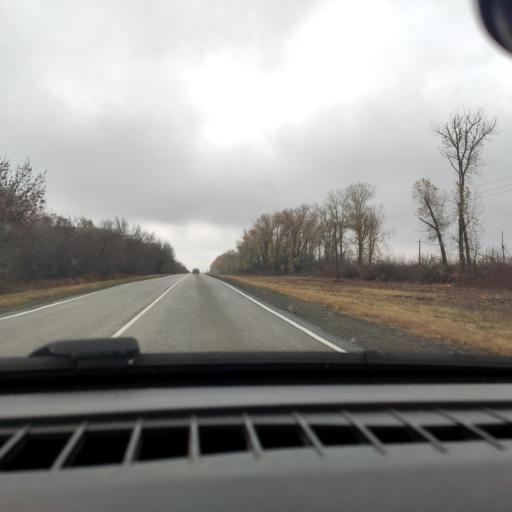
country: RU
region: Voronezj
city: Uryv-Pokrovka
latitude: 51.0849
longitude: 39.0026
